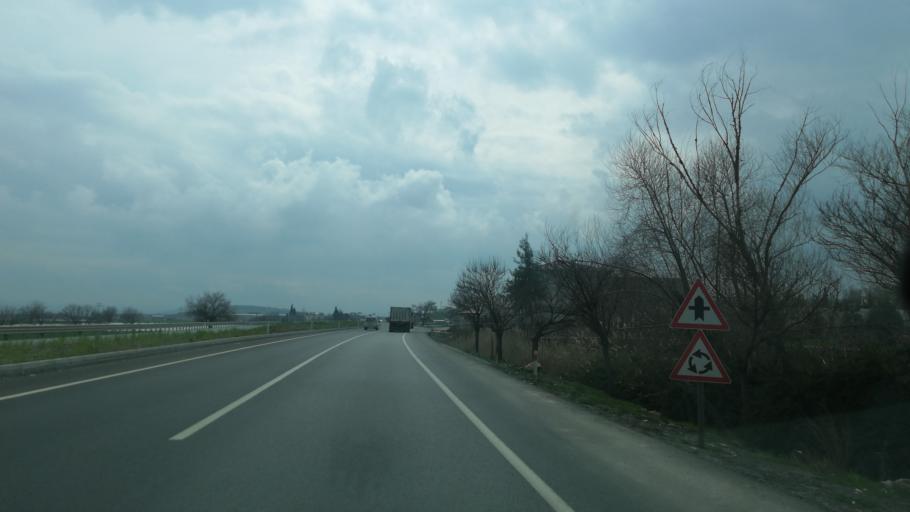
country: TR
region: Kahramanmaras
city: Turkoglu
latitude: 37.4581
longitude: 36.8890
